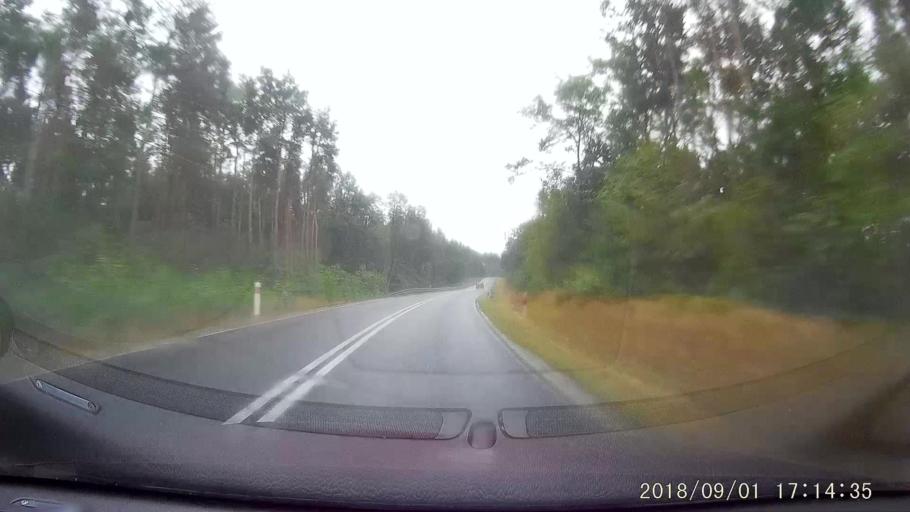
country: PL
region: Lubusz
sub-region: Powiat zielonogorski
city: Nowogrod Bobrzanski
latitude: 51.7827
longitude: 15.2589
